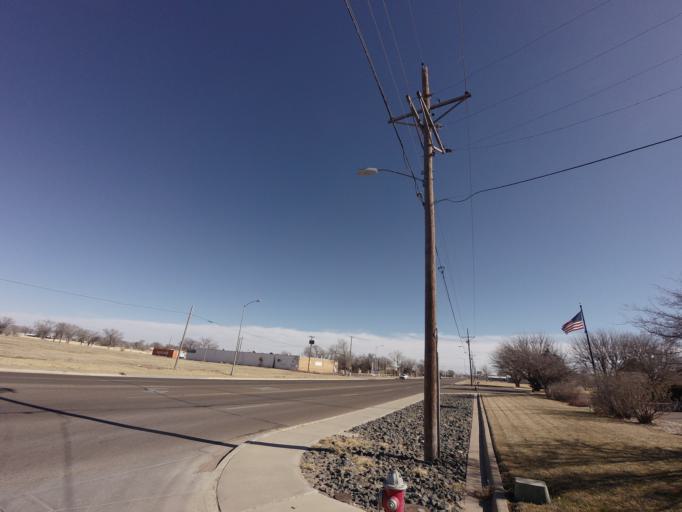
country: US
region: New Mexico
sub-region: Curry County
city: Clovis
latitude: 34.4045
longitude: -103.2365
